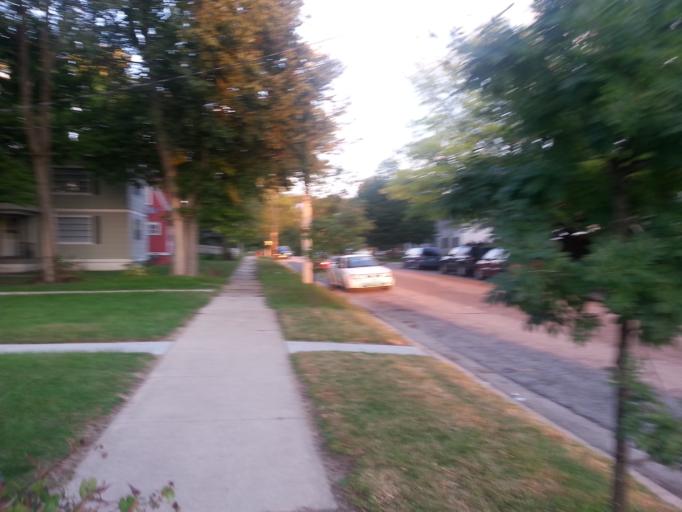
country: US
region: Minnesota
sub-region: Olmsted County
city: Rochester
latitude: 44.0324
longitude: -92.4607
